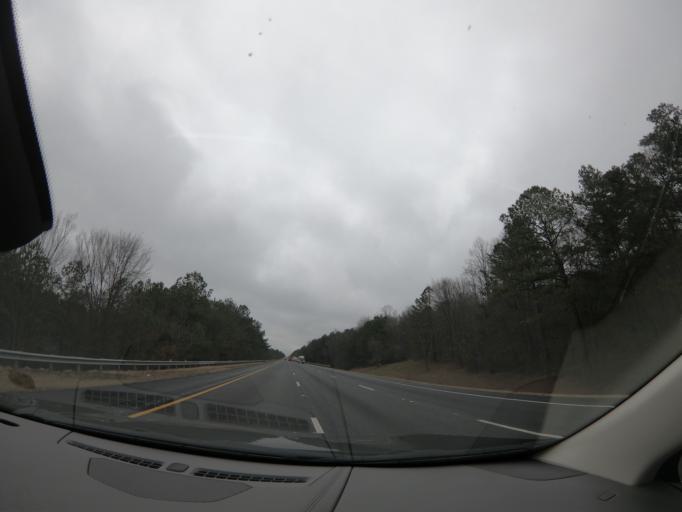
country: US
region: Georgia
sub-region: Whitfield County
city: Dalton
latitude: 34.8277
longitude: -85.0171
